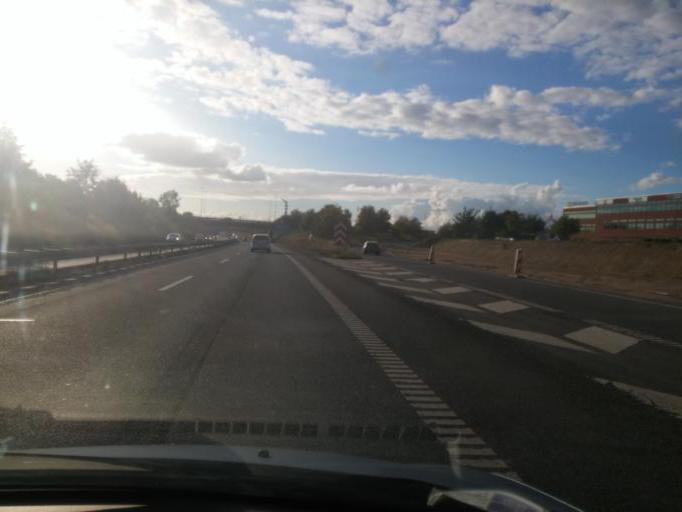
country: DK
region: South Denmark
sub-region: Odense Kommune
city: Hojby
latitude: 55.3512
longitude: 10.4117
